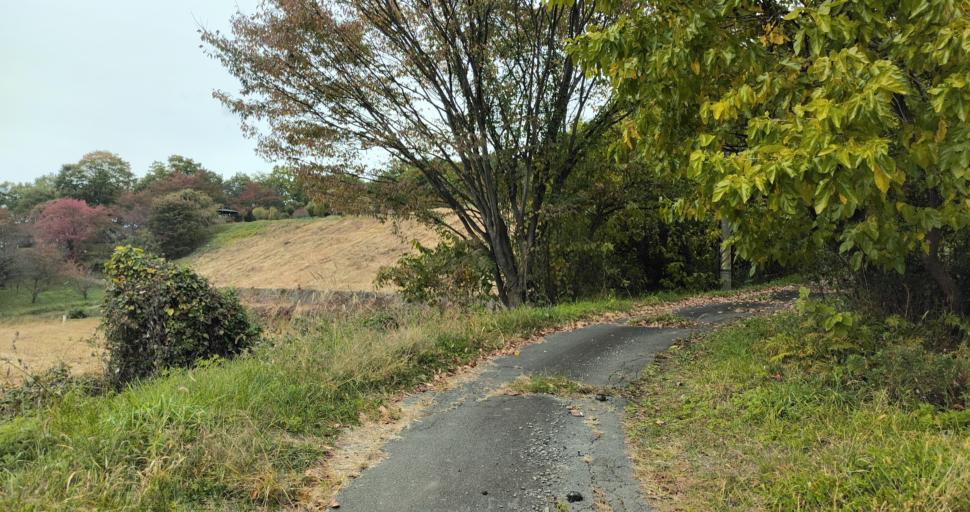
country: JP
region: Nagano
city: Komoro
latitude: 36.3630
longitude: 138.3840
